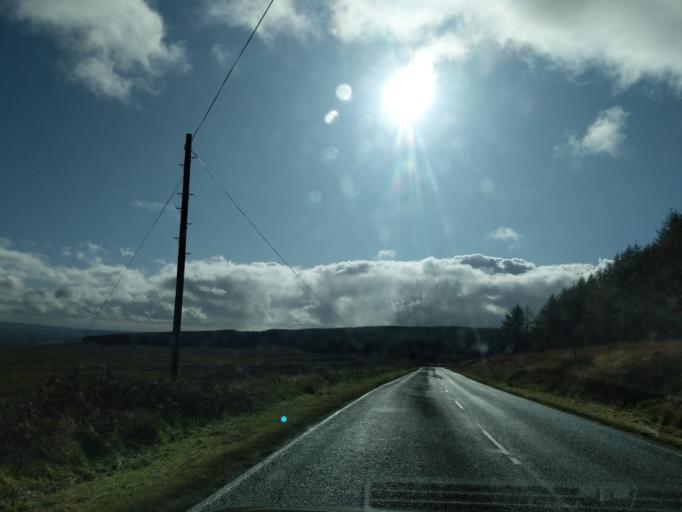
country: GB
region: Scotland
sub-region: Dumfries and Galloway
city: Moffat
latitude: 55.3902
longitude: -3.4842
